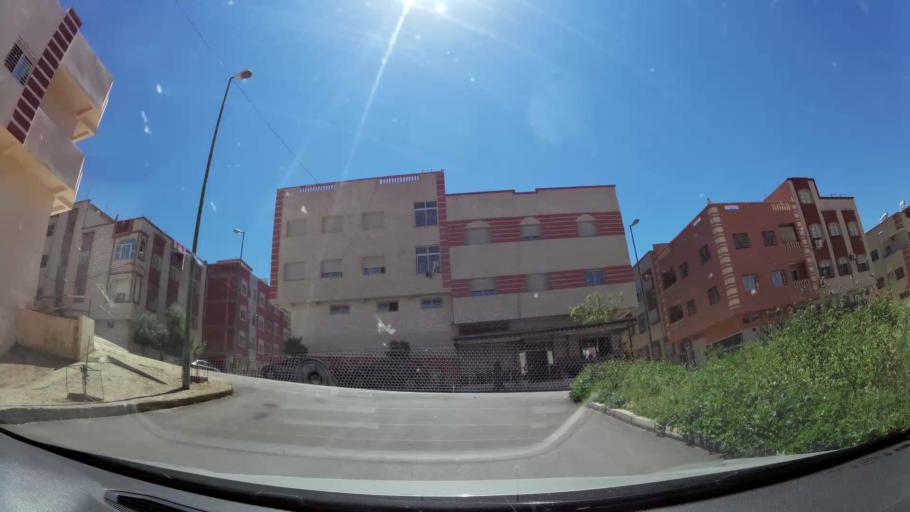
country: MA
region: Meknes-Tafilalet
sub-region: Meknes
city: Meknes
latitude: 33.8973
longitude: -5.5837
